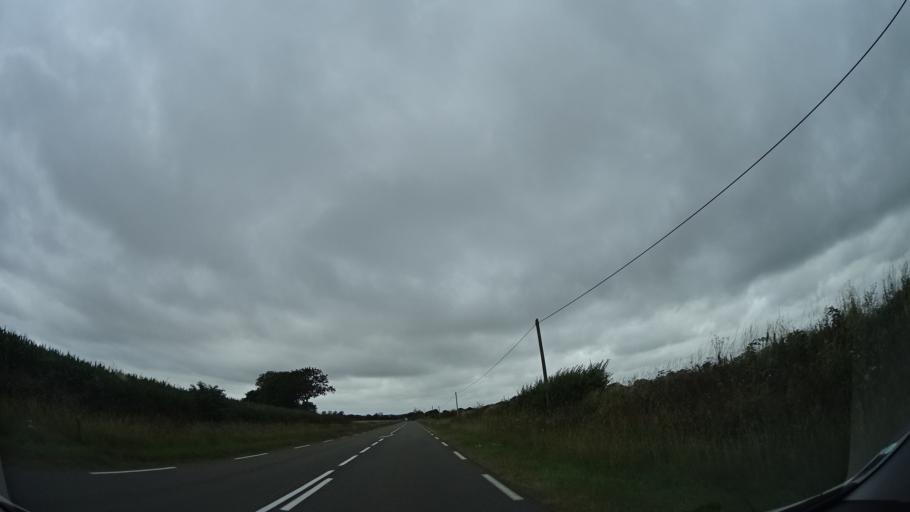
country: FR
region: Lower Normandy
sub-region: Departement de la Manche
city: La Haye-du-Puits
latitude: 49.3125
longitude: -1.6067
